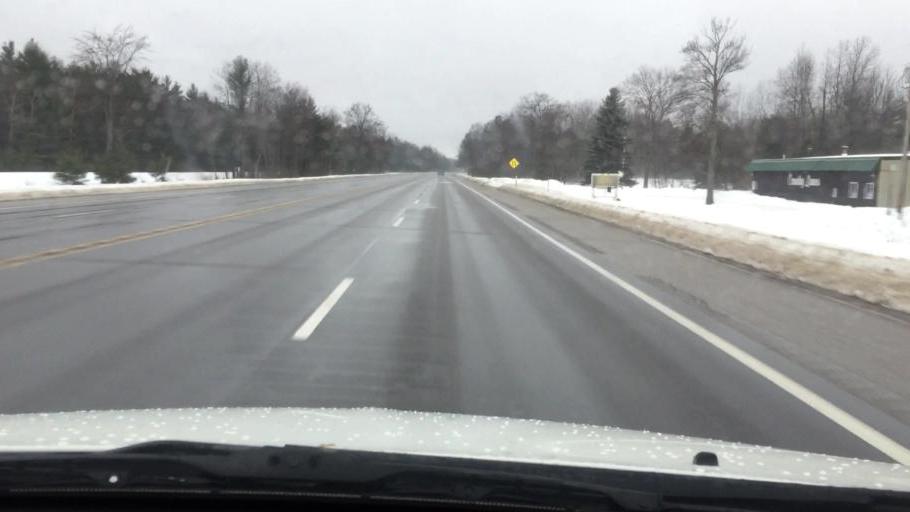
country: US
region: Michigan
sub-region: Kalkaska County
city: Kalkaska
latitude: 44.6684
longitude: -85.2430
